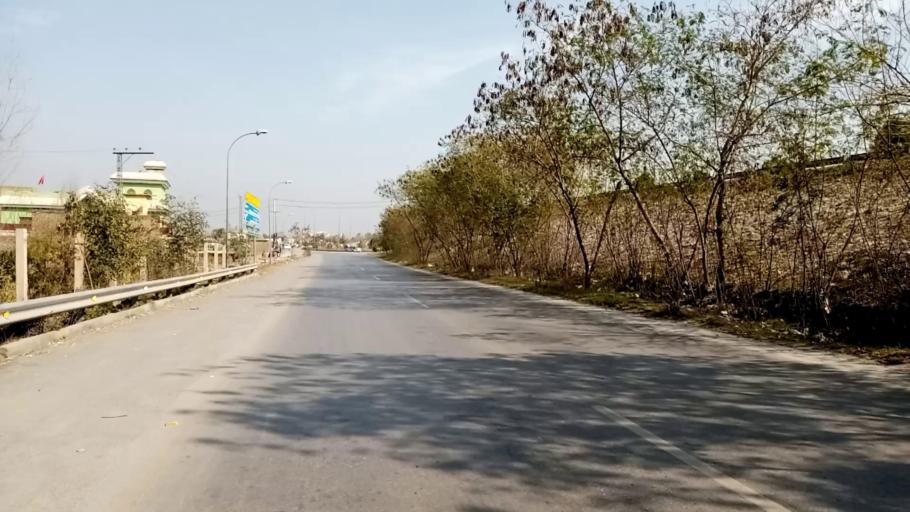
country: PK
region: Khyber Pakhtunkhwa
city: Peshawar
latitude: 34.0263
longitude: 71.6421
